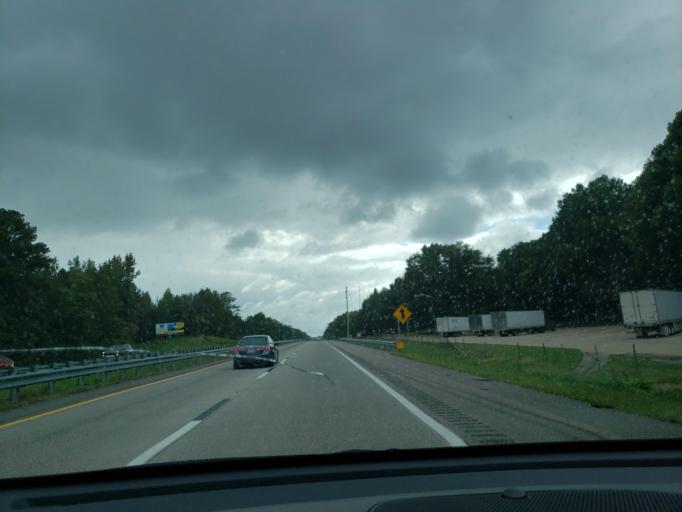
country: US
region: North Carolina
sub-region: Warren County
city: Norlina
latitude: 36.5149
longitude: -78.2059
